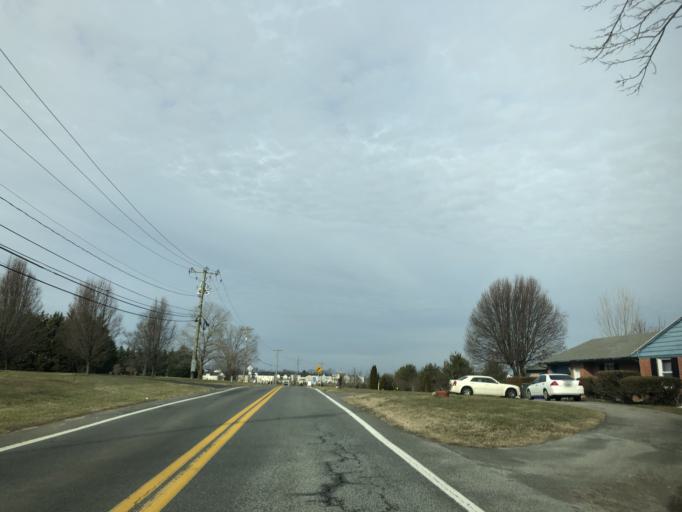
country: US
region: Delaware
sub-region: New Castle County
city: Delaware City
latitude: 39.5183
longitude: -75.6541
